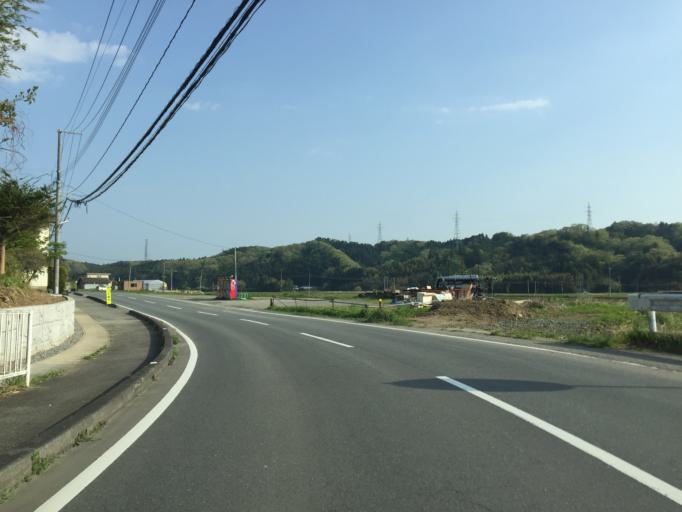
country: JP
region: Fukushima
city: Iwaki
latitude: 36.9613
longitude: 140.8166
